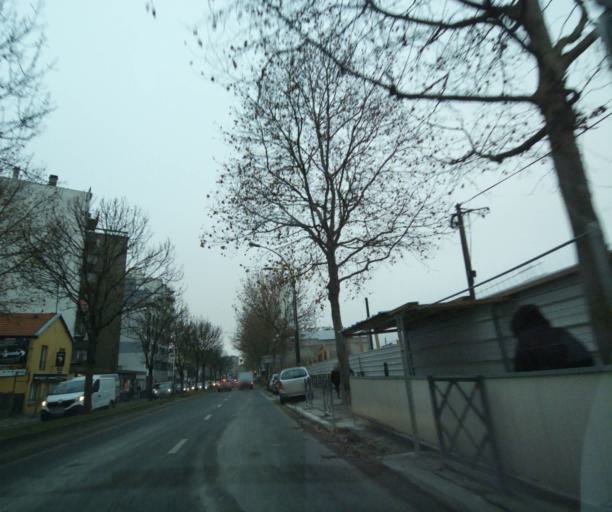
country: FR
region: Ile-de-France
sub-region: Departement de Seine-Saint-Denis
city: Le Raincy
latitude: 48.9132
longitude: 2.5239
